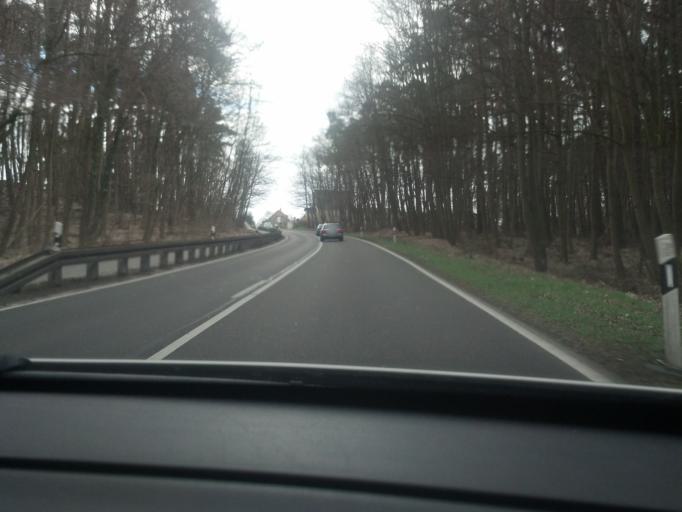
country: DE
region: Mecklenburg-Vorpommern
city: Rechlin
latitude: 53.2844
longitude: 12.7964
